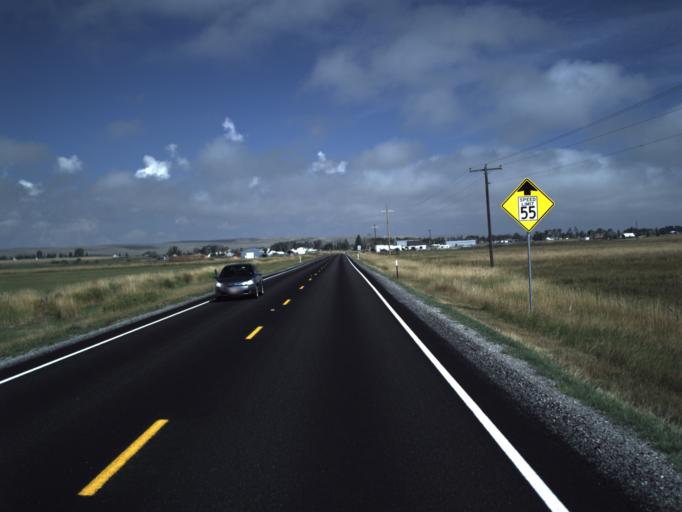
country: US
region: Utah
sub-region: Rich County
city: Randolph
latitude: 41.6480
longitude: -111.1840
